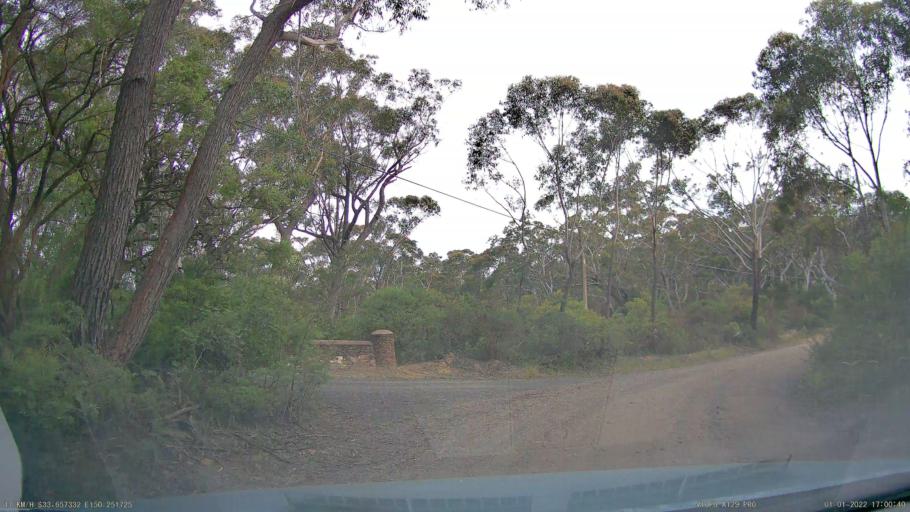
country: AU
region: New South Wales
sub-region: Blue Mountains Municipality
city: Blackheath
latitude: -33.6574
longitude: 150.2518
